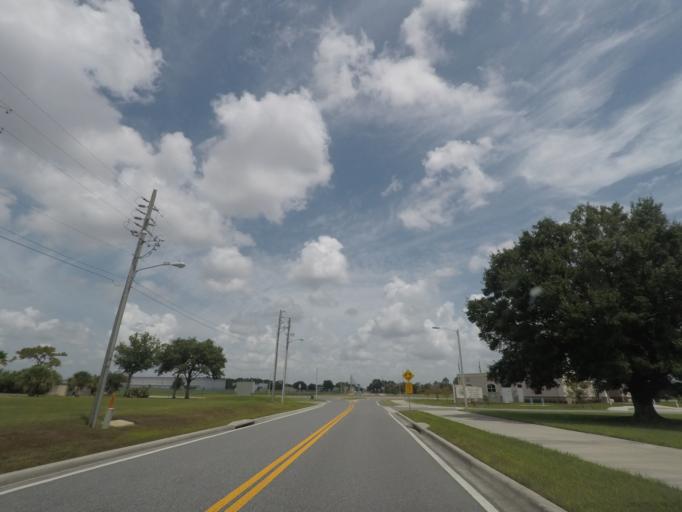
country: US
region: Florida
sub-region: Osceola County
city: Kissimmee
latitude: 28.2949
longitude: -81.4368
